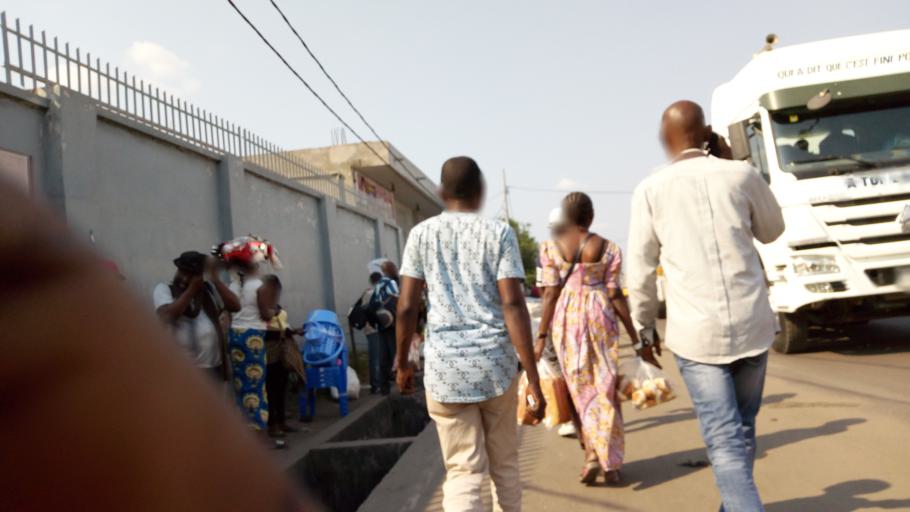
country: CD
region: Kinshasa
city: Kinshasa
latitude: -4.4509
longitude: 15.2466
